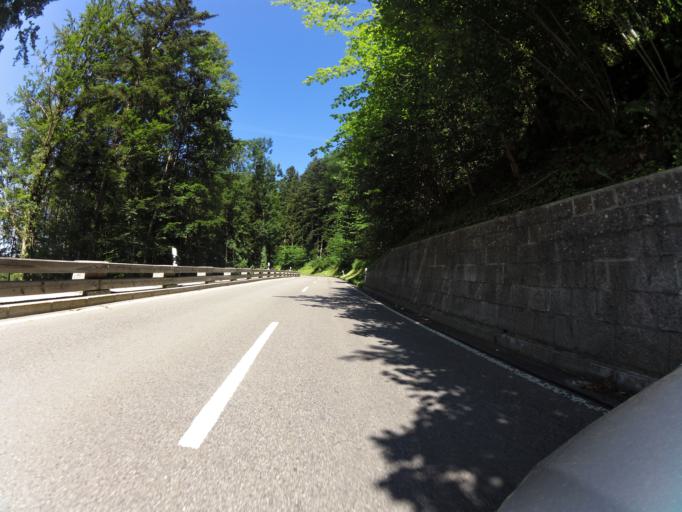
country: DE
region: Bavaria
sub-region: Upper Bavaria
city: Berchtesgaden
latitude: 47.6318
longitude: 13.0291
